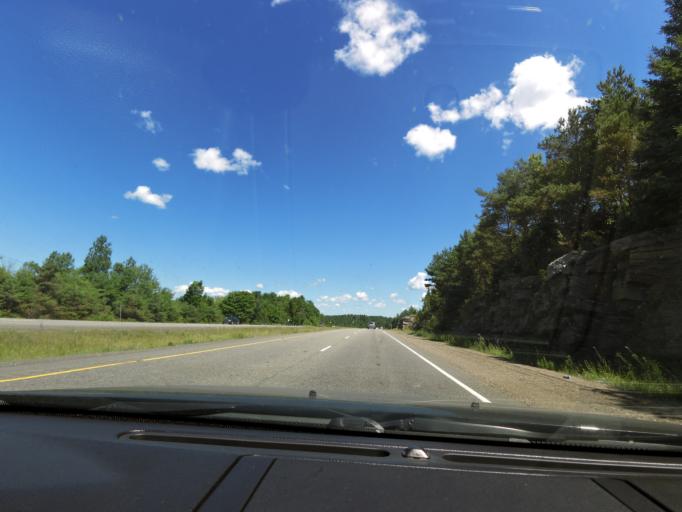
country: CA
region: Ontario
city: Bracebridge
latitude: 45.0788
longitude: -79.2965
